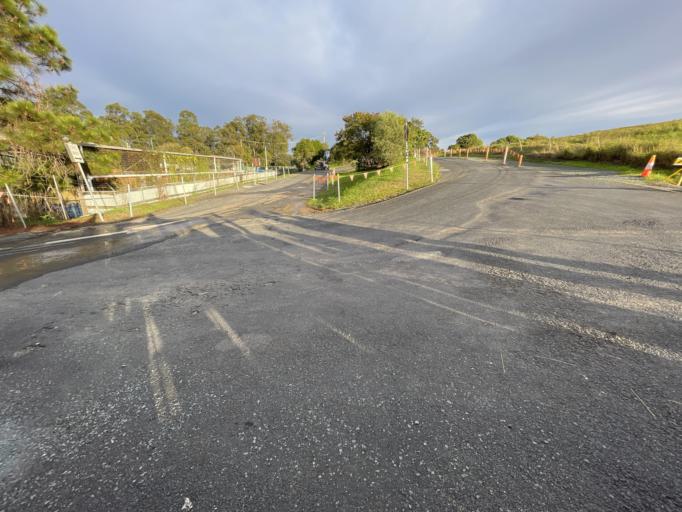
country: AU
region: Queensland
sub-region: Moreton Bay
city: Mango Hill
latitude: -27.2242
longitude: 152.9926
